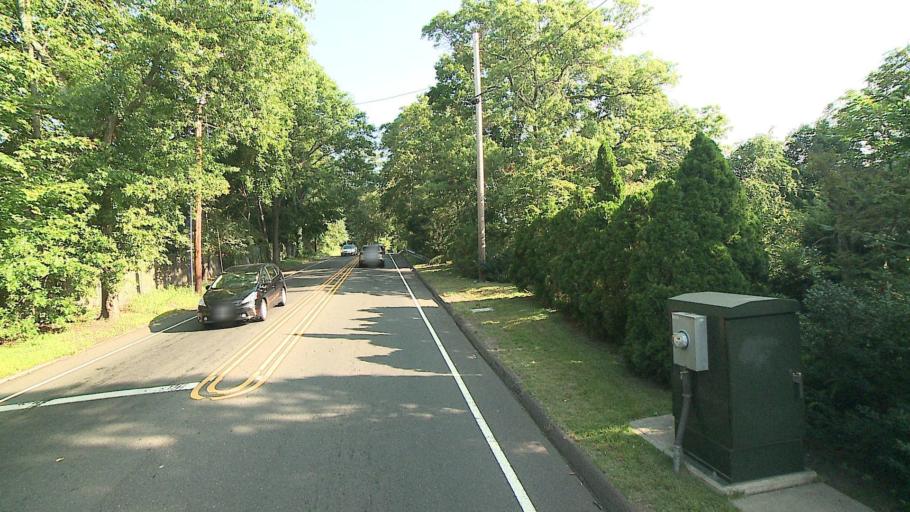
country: US
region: Connecticut
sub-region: New Haven County
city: New Haven
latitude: 41.3204
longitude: -72.9700
